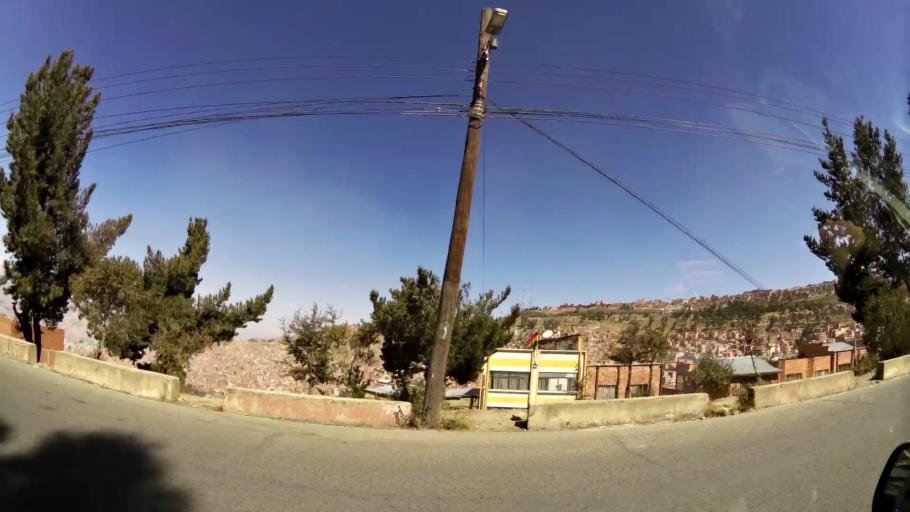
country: BO
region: La Paz
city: La Paz
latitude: -16.4868
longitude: -68.1626
